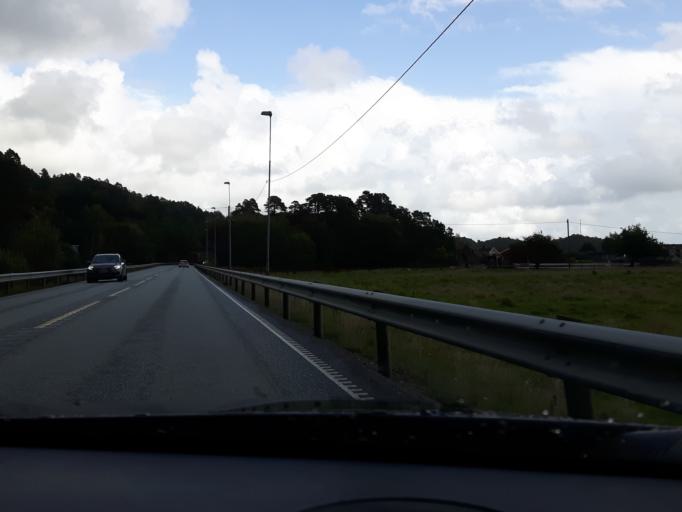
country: NO
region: Vest-Agder
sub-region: Sogne
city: Tangvall
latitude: 58.0959
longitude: 7.8011
